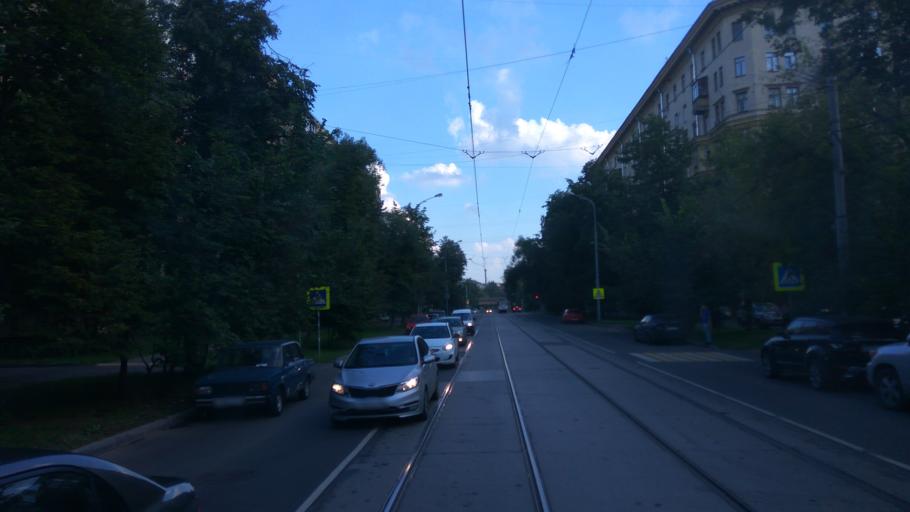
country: RU
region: Moscow
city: Likhobory
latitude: 55.8104
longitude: 37.5736
